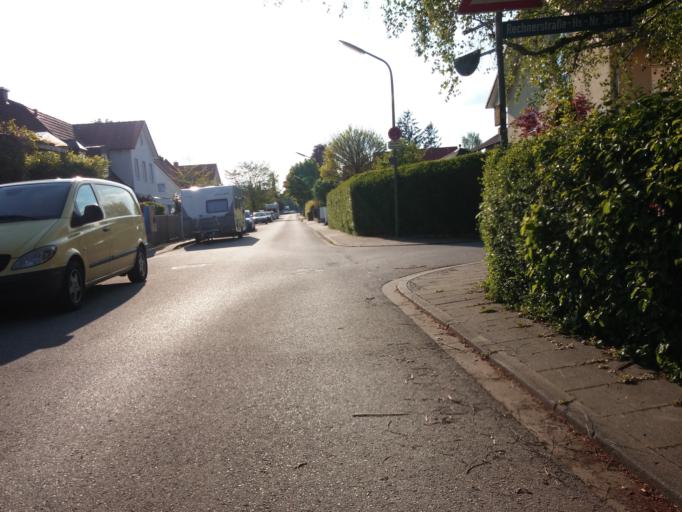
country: DE
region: Bavaria
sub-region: Upper Bavaria
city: Vaterstetten
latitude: 48.1047
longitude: 11.7483
